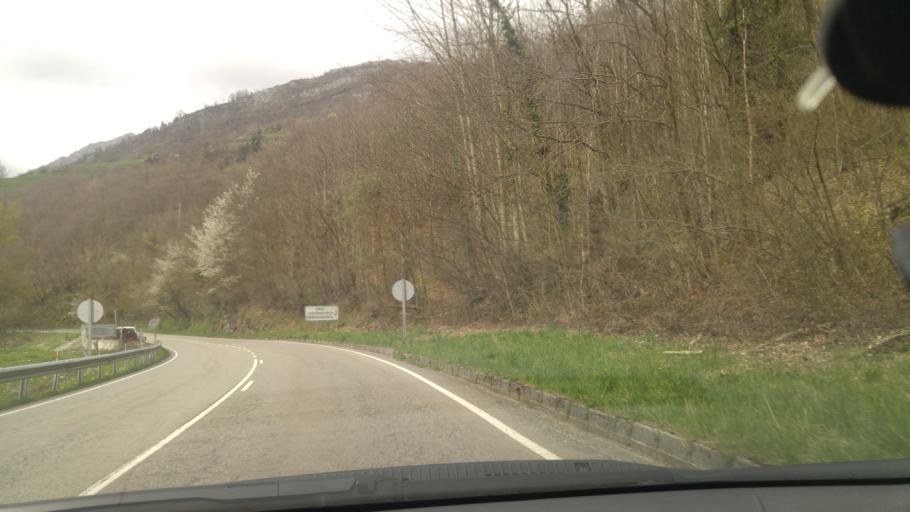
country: ES
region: Asturias
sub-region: Province of Asturias
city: Rio Aller
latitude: 43.1287
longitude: -5.5659
